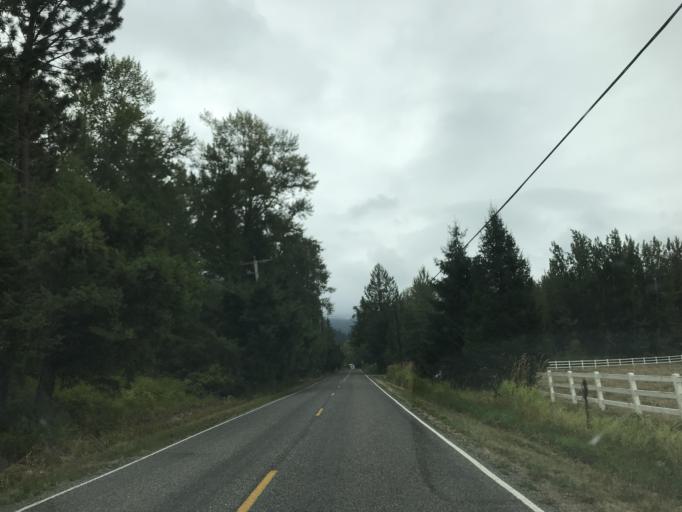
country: US
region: Washington
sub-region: Whatcom County
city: Sudden Valley
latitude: 48.8010
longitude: -122.3357
